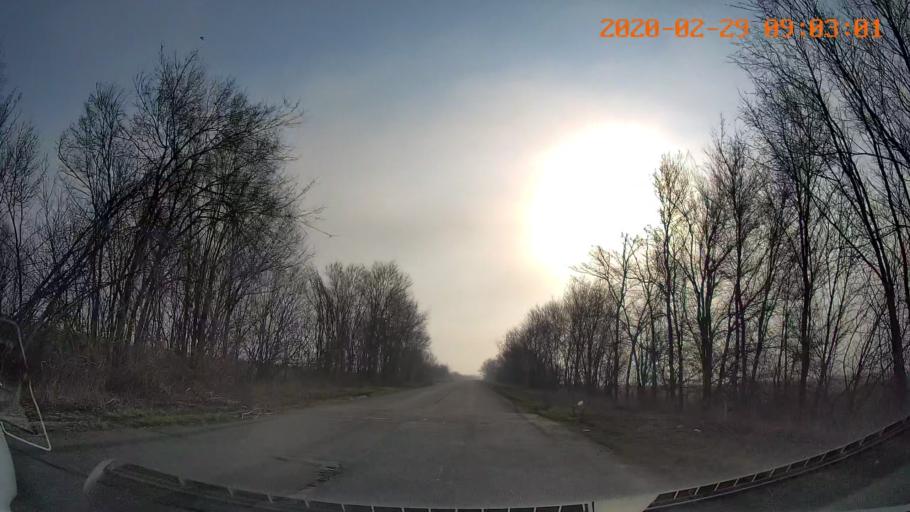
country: UA
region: Odessa
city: Velykoploske
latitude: 46.9181
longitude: 29.7211
